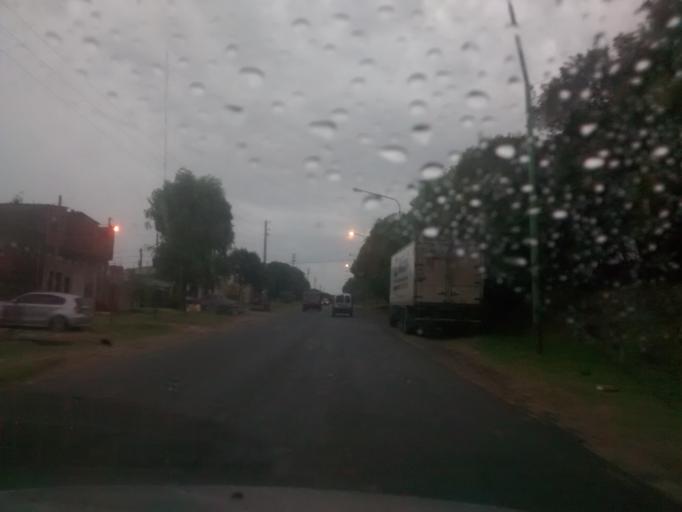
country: AR
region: Buenos Aires
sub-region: Partido de La Plata
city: La Plata
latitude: -34.9110
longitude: -58.0096
